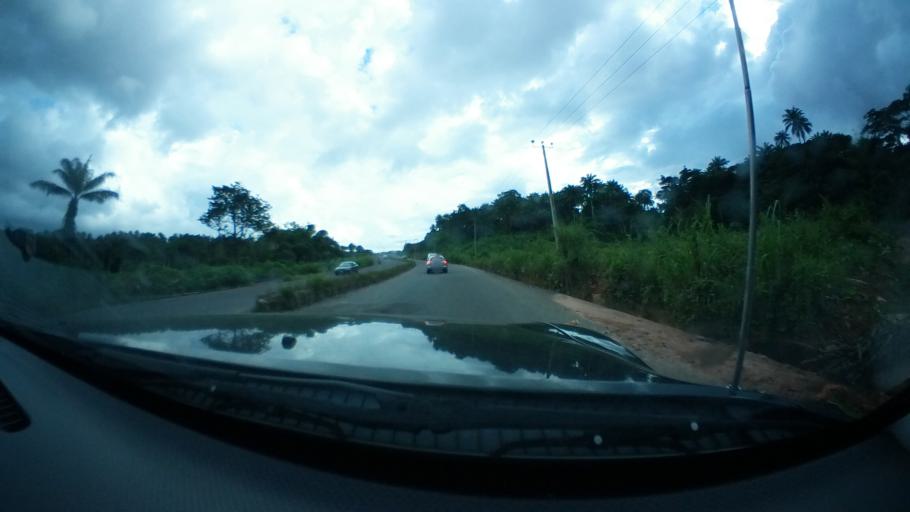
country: NG
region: Imo
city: Orlu
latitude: 5.8019
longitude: 7.0436
